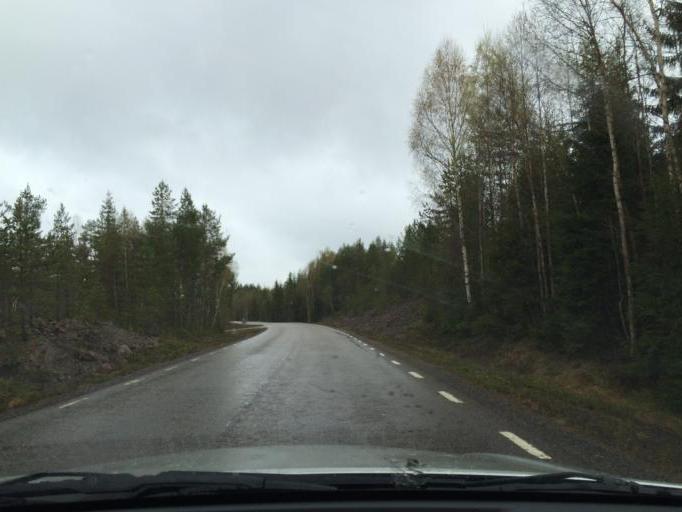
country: SE
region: Dalarna
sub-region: Ludvika Kommun
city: Abborrberget
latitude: 60.0614
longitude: 14.8082
